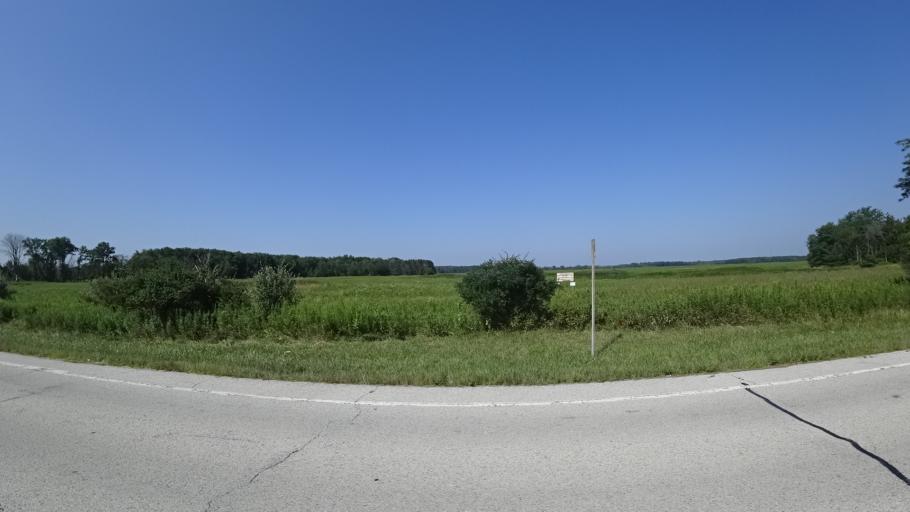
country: US
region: Illinois
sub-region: Cook County
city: Matteson
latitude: 41.5313
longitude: -87.7517
